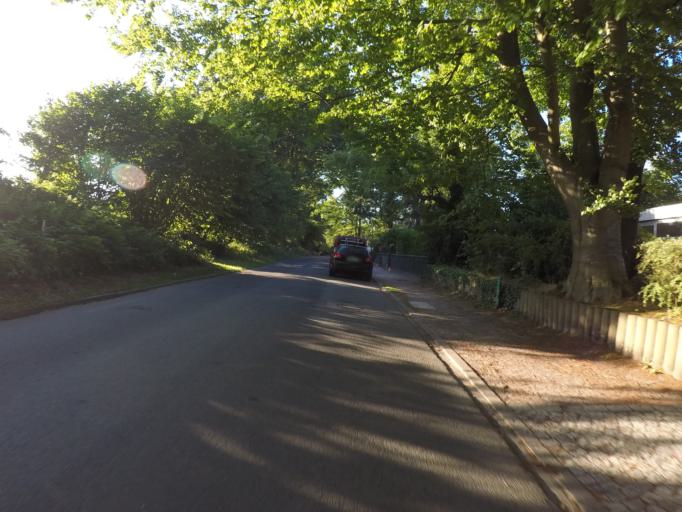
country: DE
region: Hamburg
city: Wohldorf-Ohlstedt
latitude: 53.6880
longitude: 10.1147
